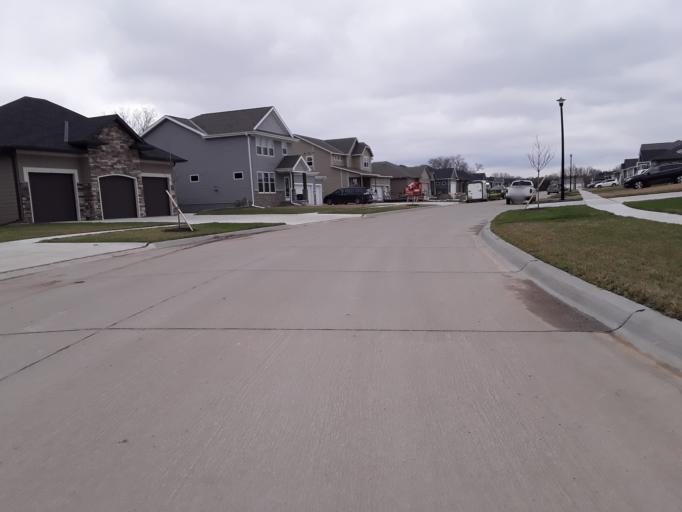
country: US
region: Nebraska
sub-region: Lancaster County
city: Lincoln
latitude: 40.8457
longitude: -96.5922
